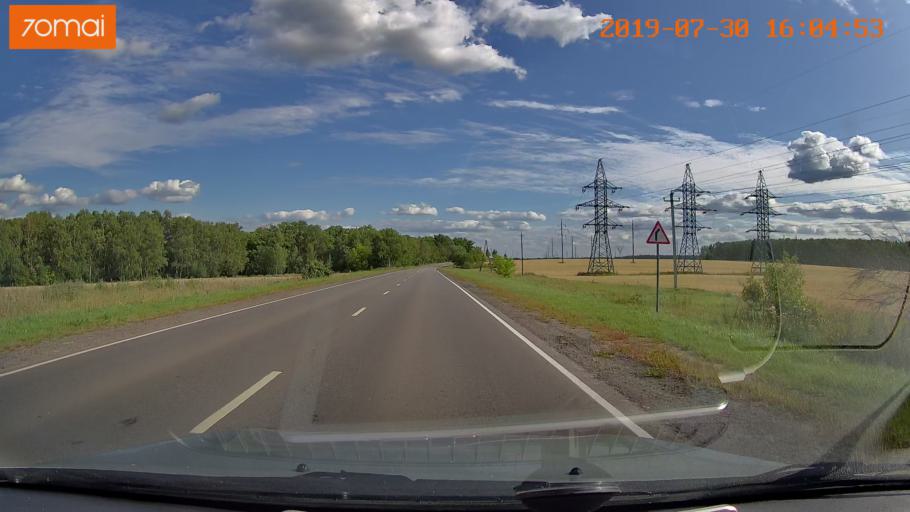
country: RU
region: Moskovskaya
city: Lopatinskiy
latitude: 55.2744
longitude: 38.7117
